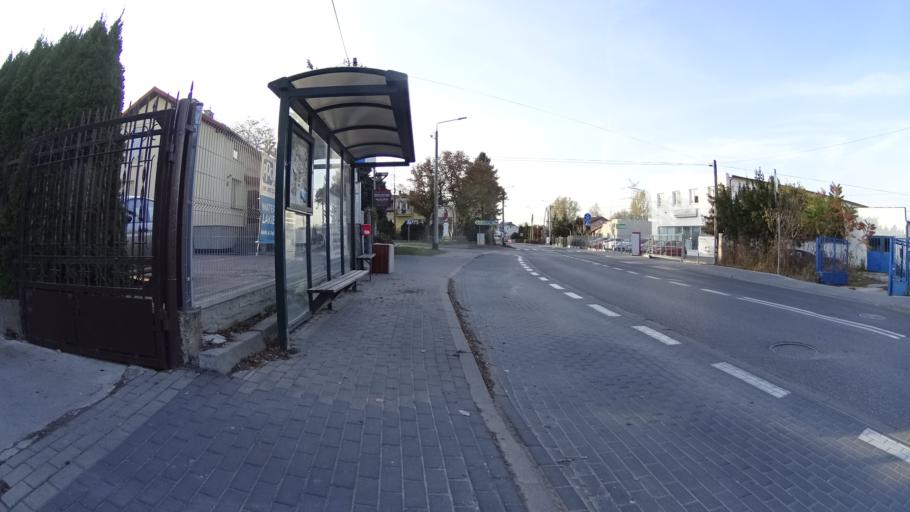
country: PL
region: Masovian Voivodeship
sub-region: Powiat warszawski zachodni
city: Babice
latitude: 52.2881
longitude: 20.8698
